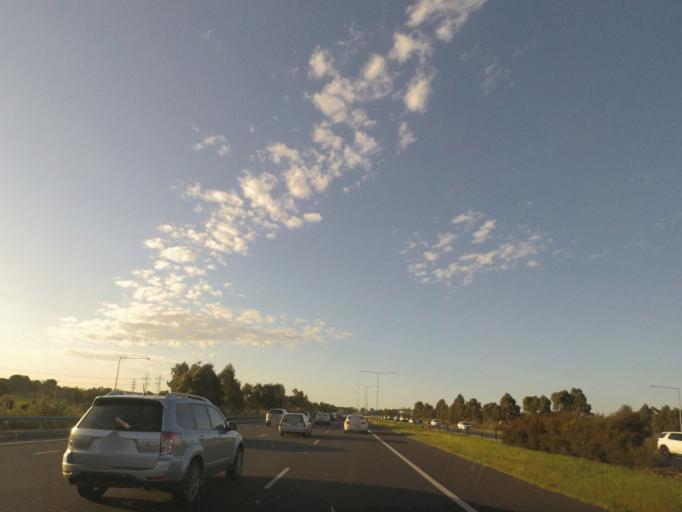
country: AU
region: Victoria
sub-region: Knox
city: Scoresby
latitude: -37.9054
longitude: 145.2156
